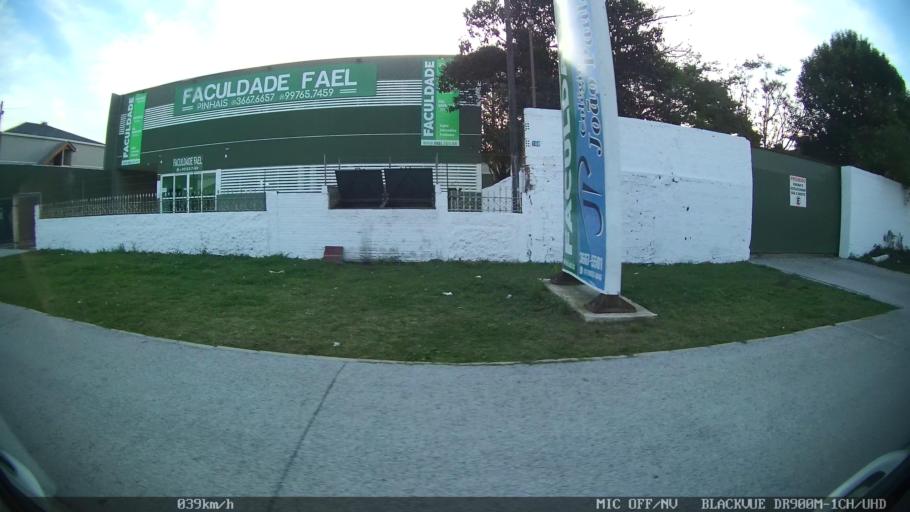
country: BR
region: Parana
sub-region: Pinhais
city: Pinhais
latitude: -25.4518
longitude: -49.1811
